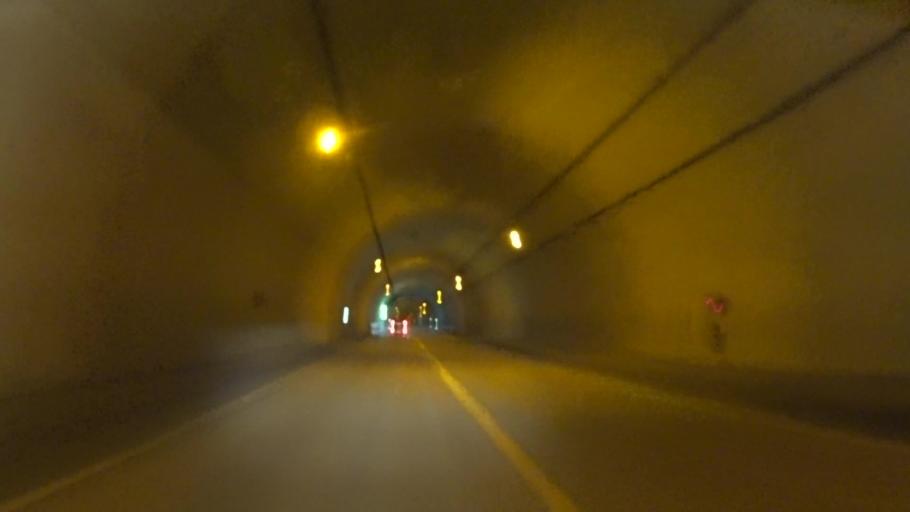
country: JP
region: Kyoto
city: Fukuchiyama
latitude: 35.4022
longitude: 135.0382
